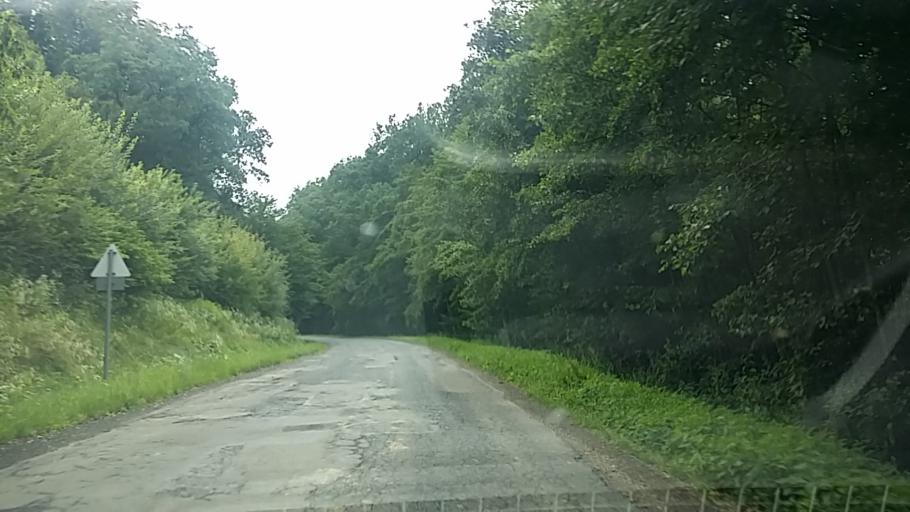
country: HR
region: Medimurska
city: Domasinec
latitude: 46.4927
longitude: 16.6591
